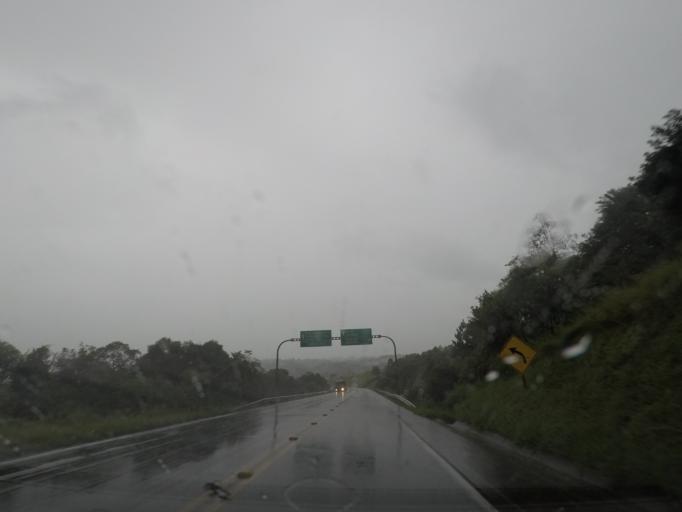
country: BR
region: Parana
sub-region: Almirante Tamandare
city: Almirante Tamandare
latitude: -25.3539
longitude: -49.2891
